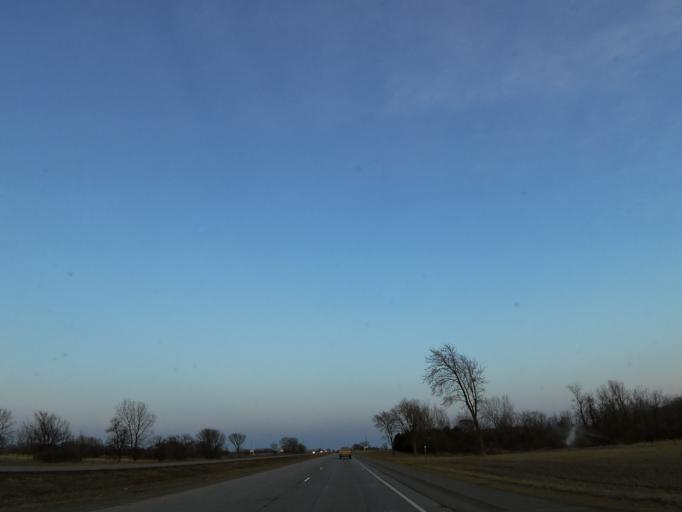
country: US
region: Minnesota
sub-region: Mower County
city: Austin
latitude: 43.6713
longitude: -92.9080
